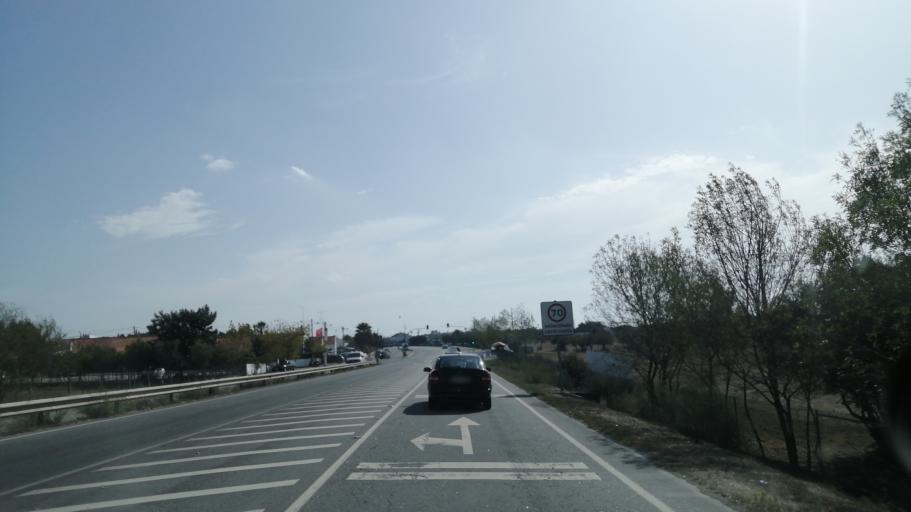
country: PT
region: Evora
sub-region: Evora
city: Evora
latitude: 38.5677
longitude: -7.9571
